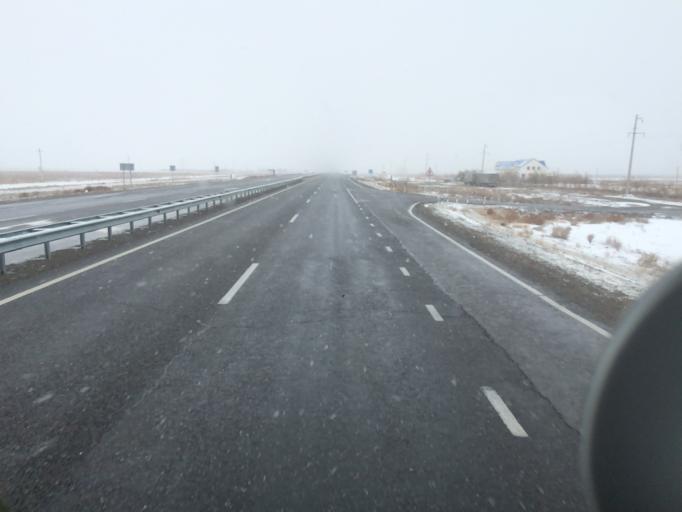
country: KZ
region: Ongtustik Qazaqstan
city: Turkestan
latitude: 43.4567
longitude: 67.9350
